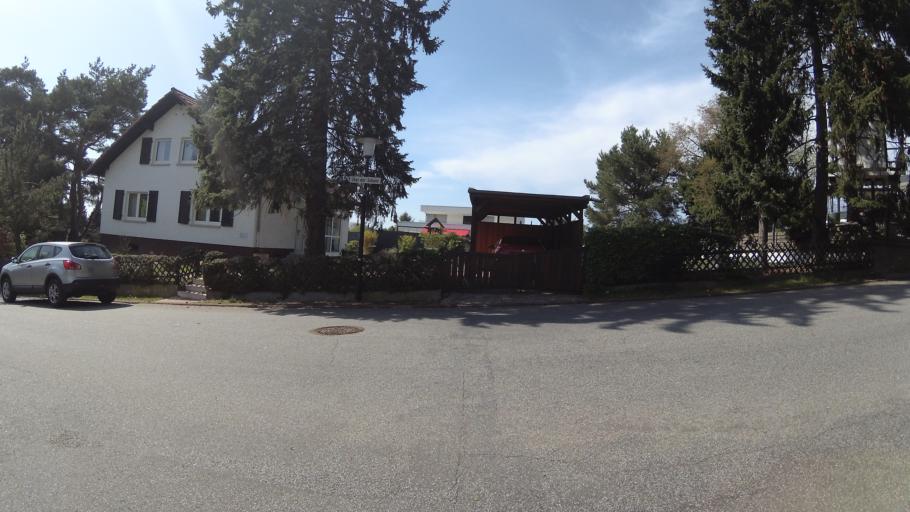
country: DE
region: Rheinland-Pfalz
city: Bechhofen
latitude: 49.3411
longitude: 7.3717
